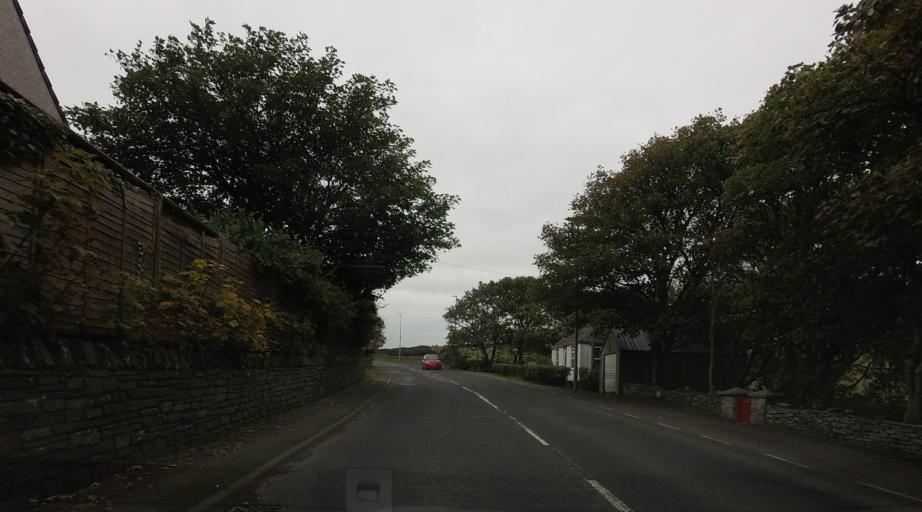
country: GB
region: Scotland
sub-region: Orkney Islands
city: Orkney
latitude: 59.0084
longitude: -3.1238
